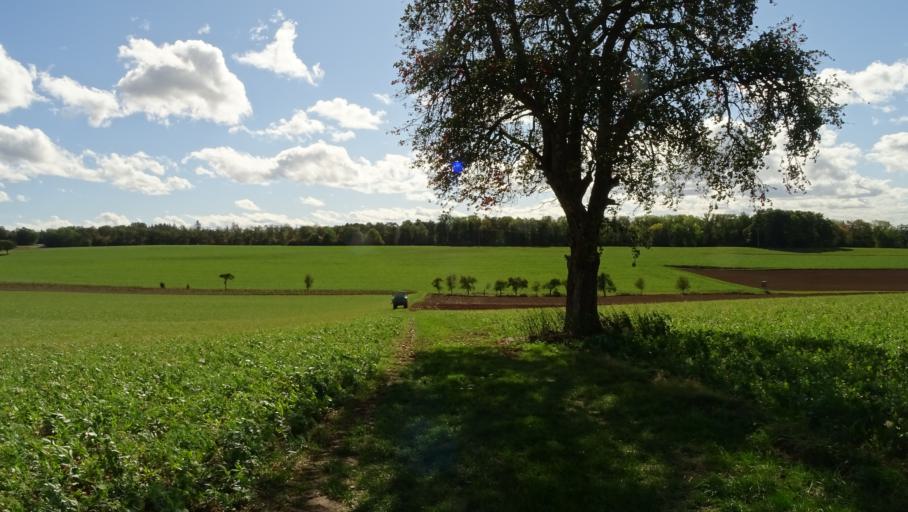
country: DE
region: Baden-Wuerttemberg
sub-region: Karlsruhe Region
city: Neckargerach
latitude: 49.3907
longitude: 9.0953
